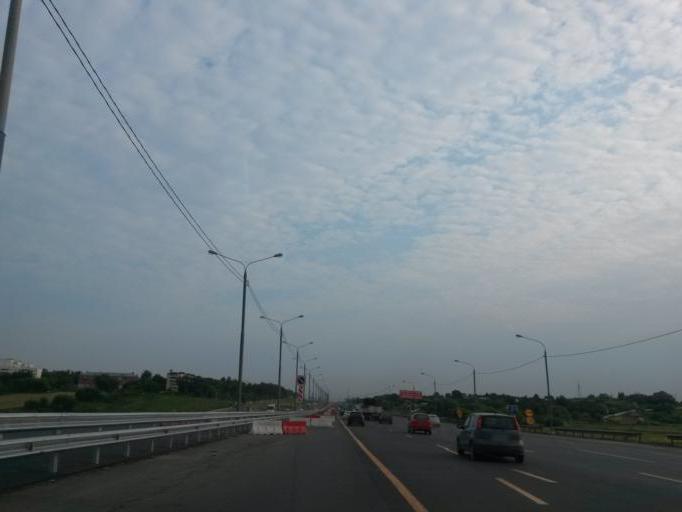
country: RU
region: Moskovskaya
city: Shcherbinka
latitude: 55.4671
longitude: 37.6183
